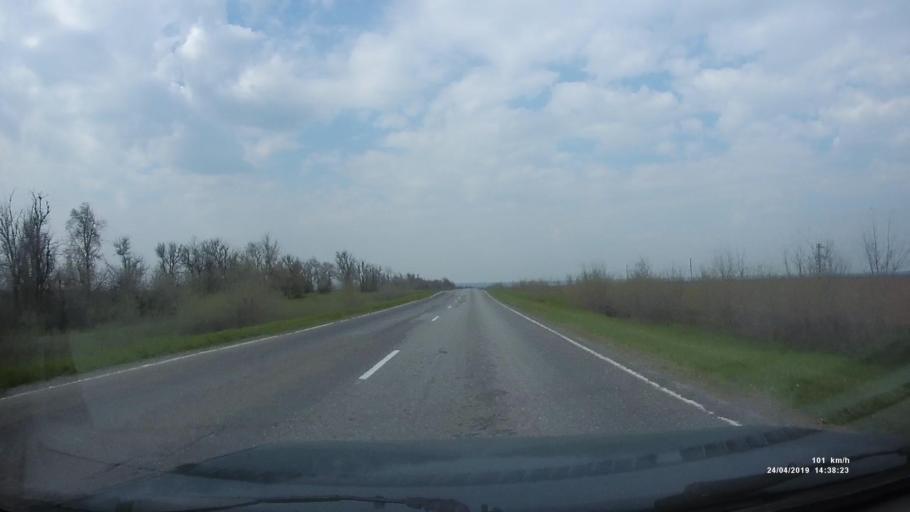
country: RU
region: Rostov
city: Remontnoye
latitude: 46.4005
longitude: 43.8861
